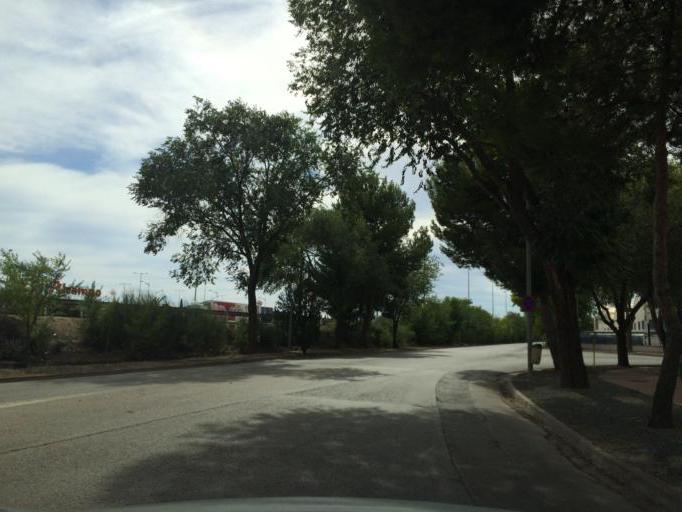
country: ES
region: Castille-La Mancha
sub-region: Provincia de Albacete
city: Albacete
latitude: 39.0115
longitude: -1.8772
